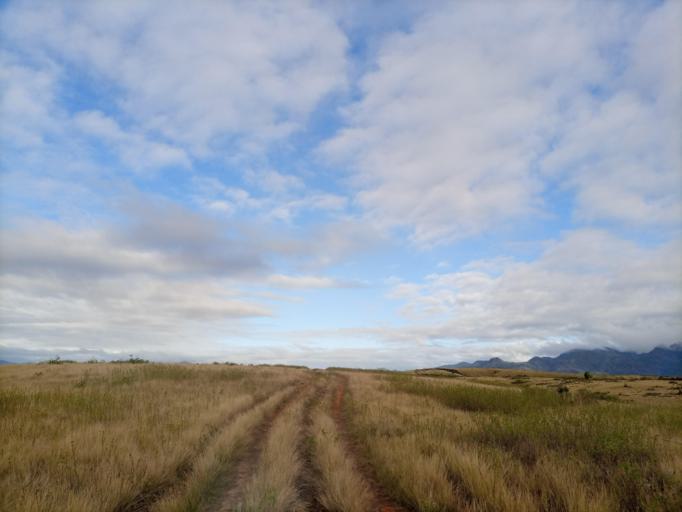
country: MG
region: Anosy
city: Fort Dauphin
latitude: -24.3104
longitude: 47.2439
